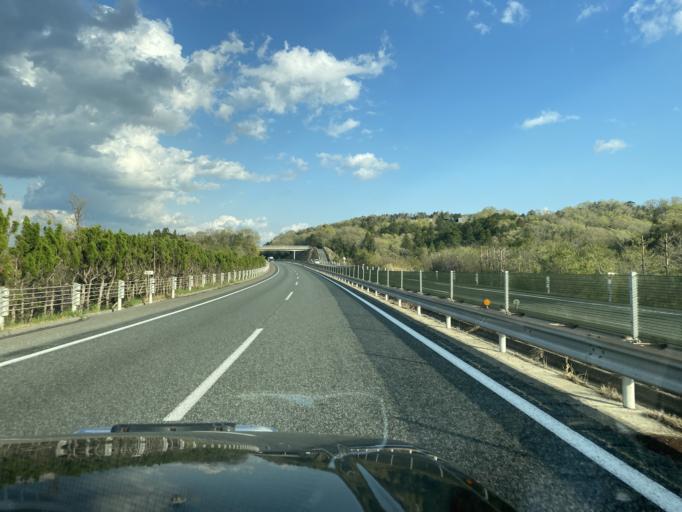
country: JP
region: Hyogo
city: Sandacho
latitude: 34.9471
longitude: 135.1432
